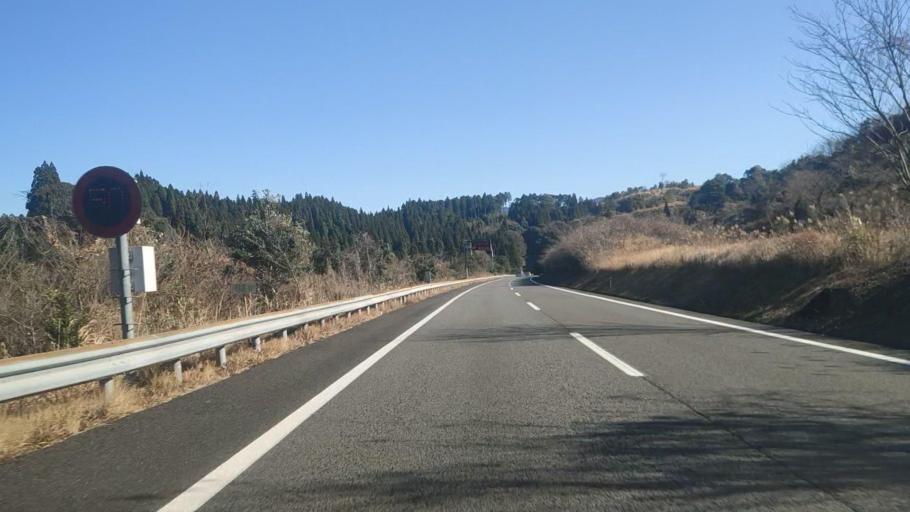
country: JP
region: Miyazaki
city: Miyazaki-shi
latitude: 31.8222
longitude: 131.2520
